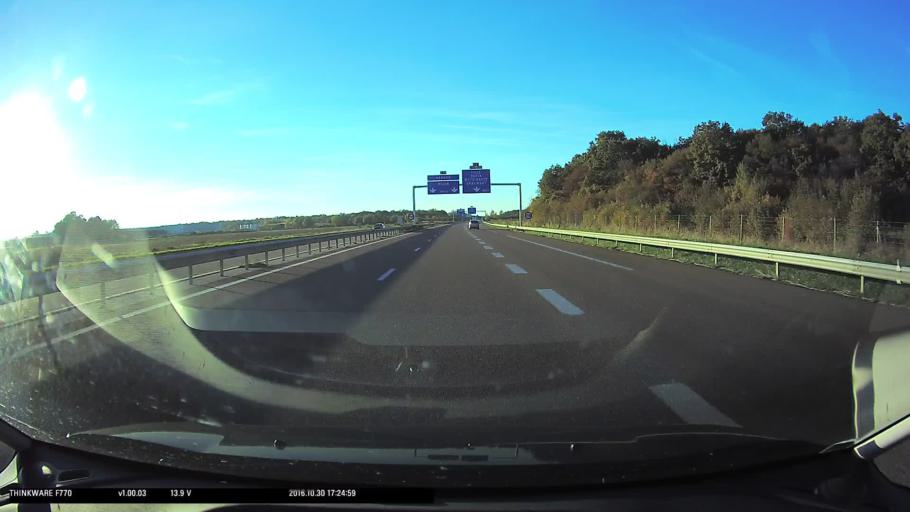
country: FR
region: Bourgogne
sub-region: Departement de la Cote-d'Or
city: Chevigny-Saint-Sauveur
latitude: 47.2718
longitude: 5.1545
